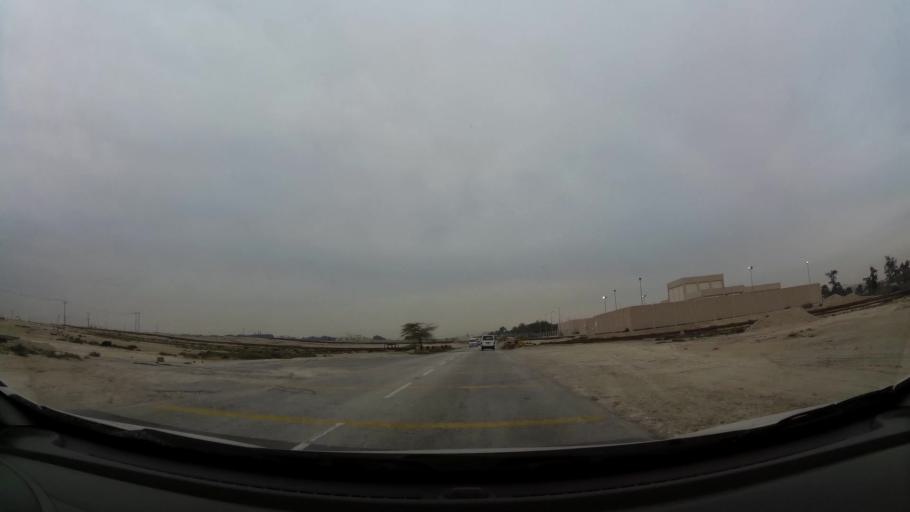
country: BH
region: Northern
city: Ar Rifa'
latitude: 26.0889
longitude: 50.5712
